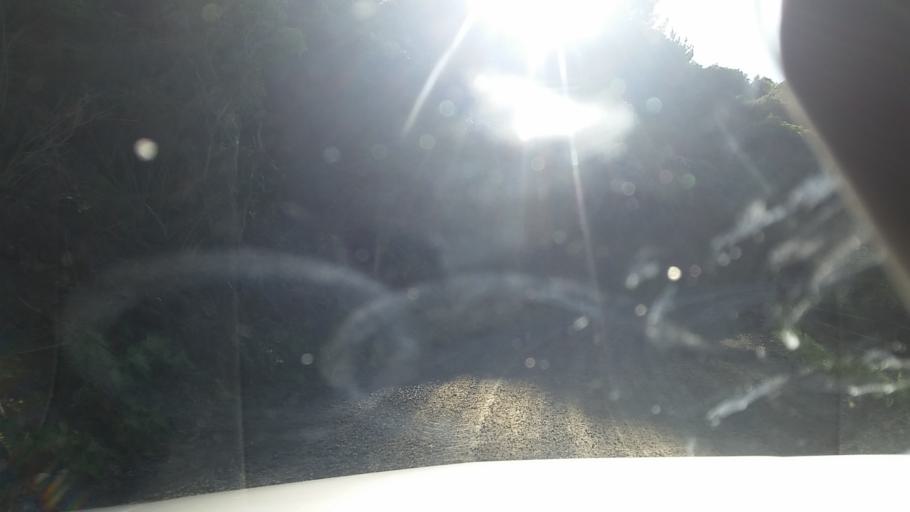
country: NZ
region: Marlborough
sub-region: Marlborough District
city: Blenheim
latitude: -41.4454
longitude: 173.8832
